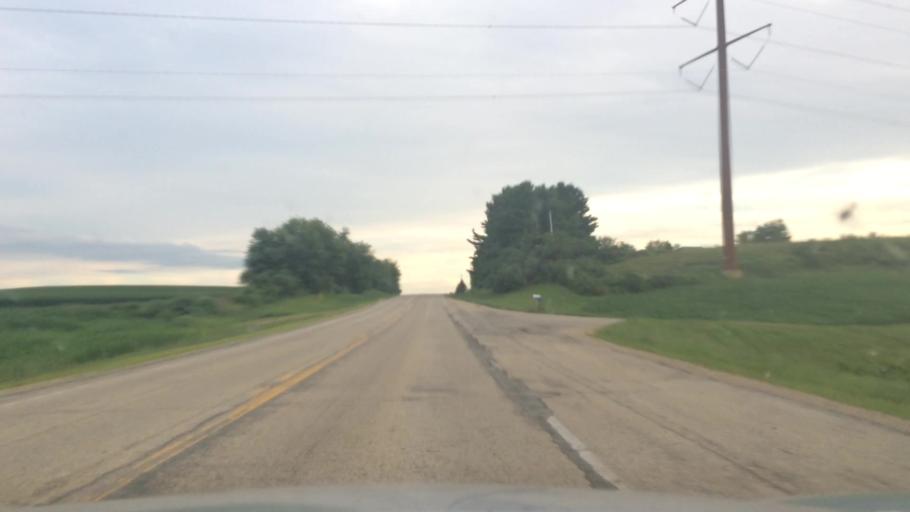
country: US
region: Wisconsin
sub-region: Columbia County
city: Lodi
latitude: 43.2292
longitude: -89.5423
